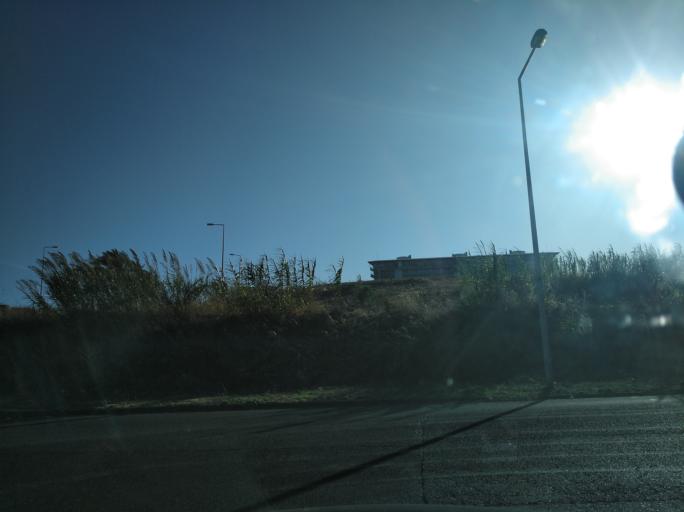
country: PT
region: Lisbon
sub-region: Loures
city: Moscavide
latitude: 38.7502
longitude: -9.1204
